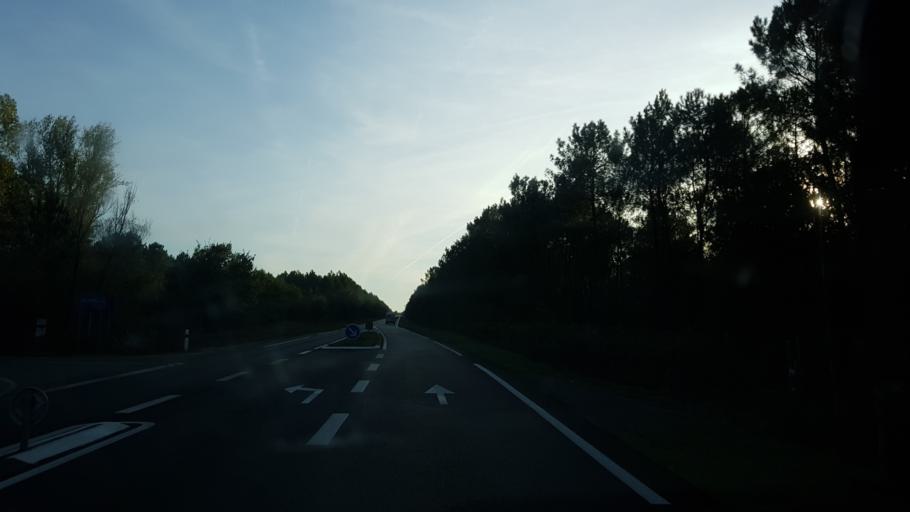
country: FR
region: Aquitaine
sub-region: Departement de la Gironde
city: Martignas-sur-Jalle
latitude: 44.8217
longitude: -0.8498
